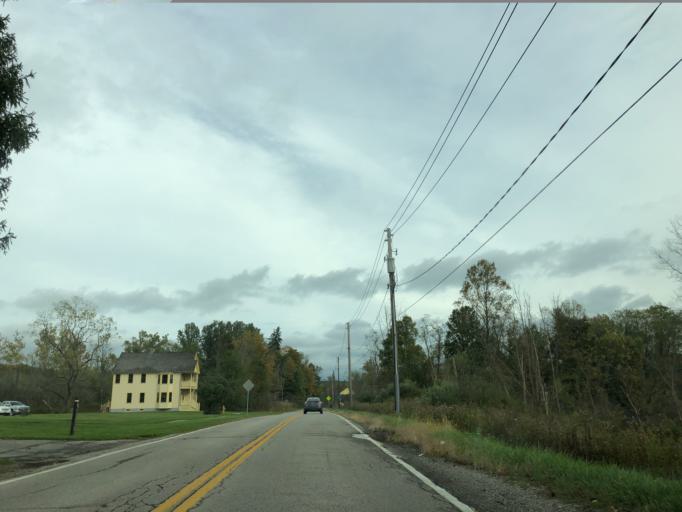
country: US
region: Ohio
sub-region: Summit County
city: Peninsula
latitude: 41.2858
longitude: -81.5738
